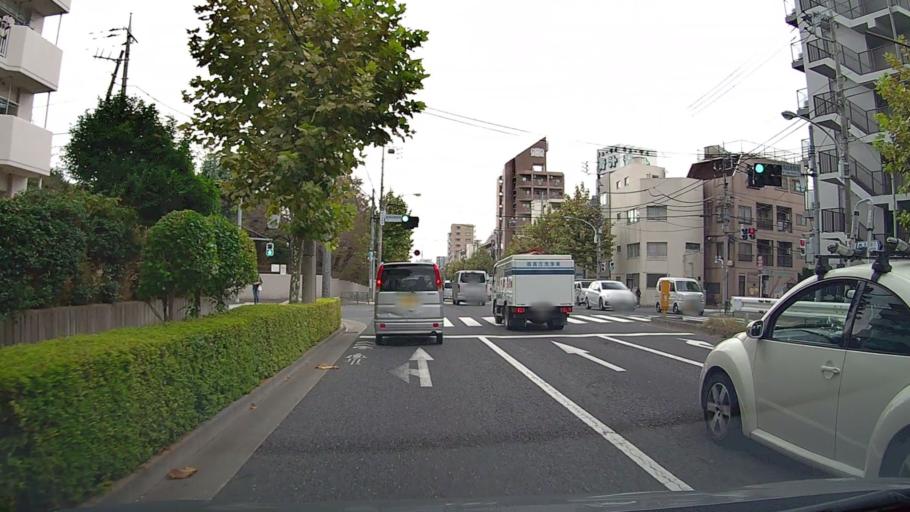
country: JP
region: Saitama
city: Wako
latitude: 35.7603
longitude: 139.6572
